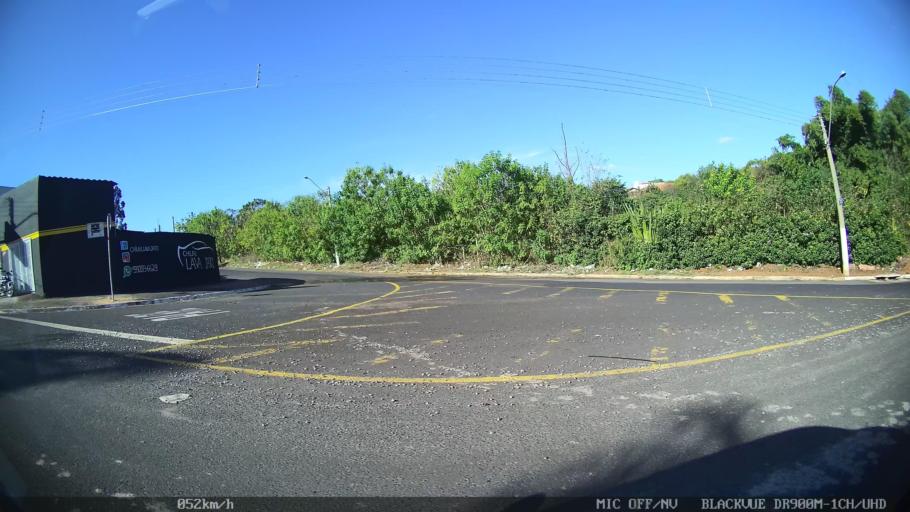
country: BR
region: Sao Paulo
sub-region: Franca
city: Franca
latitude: -20.4884
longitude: -47.4287
